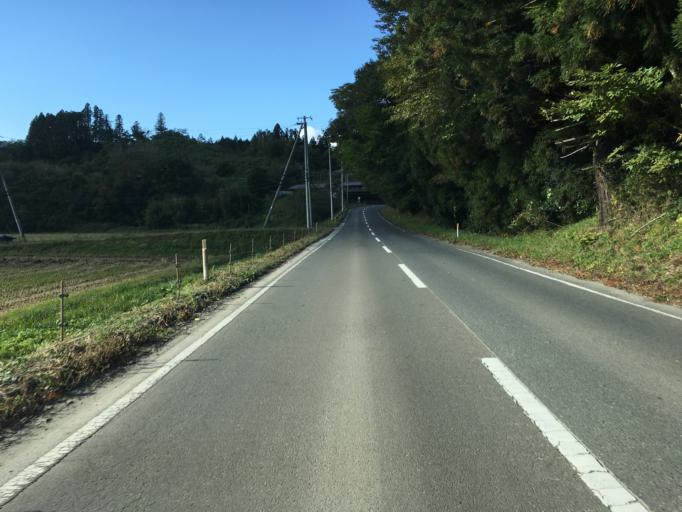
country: JP
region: Miyagi
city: Marumori
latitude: 37.8542
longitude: 140.8310
